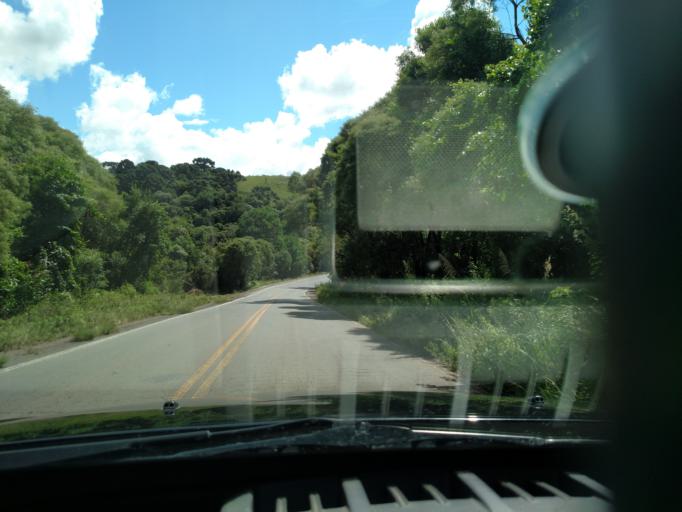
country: BR
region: Santa Catarina
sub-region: Lages
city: Lages
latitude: -27.8674
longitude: -50.1835
